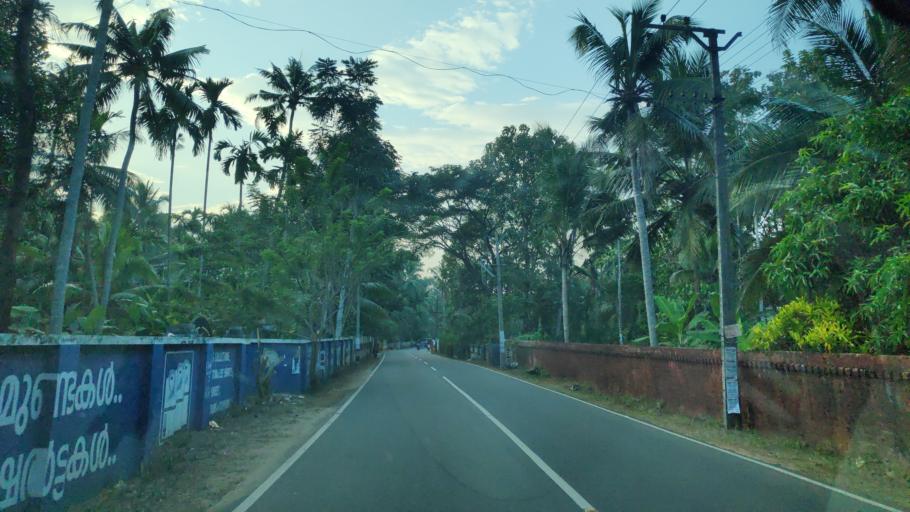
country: IN
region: Kerala
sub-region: Alappuzha
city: Shertallai
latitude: 9.6808
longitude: 76.3705
